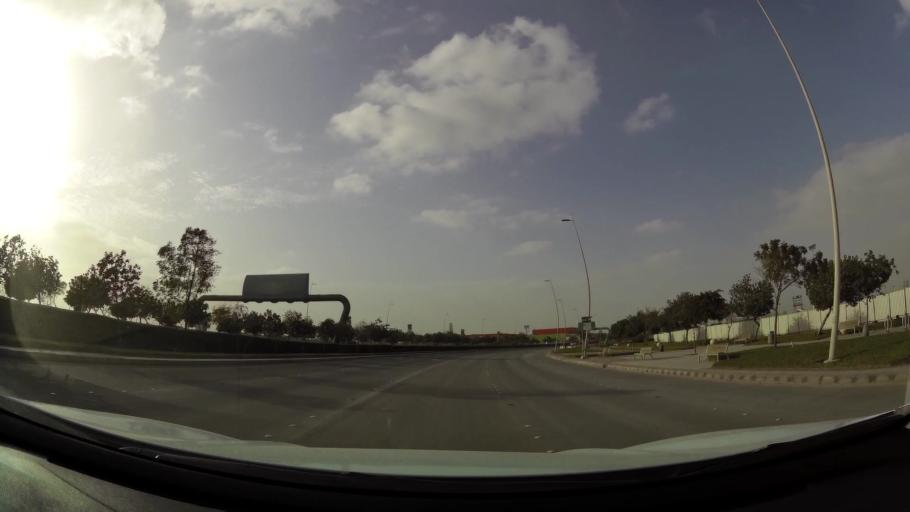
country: AE
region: Abu Dhabi
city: Abu Dhabi
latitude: 24.4915
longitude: 54.5918
